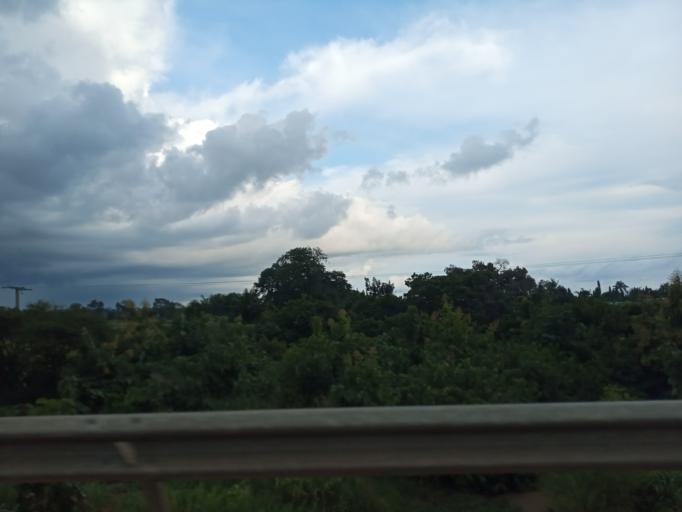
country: TG
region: Centrale
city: Sotouboua
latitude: 8.5806
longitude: 0.9853
